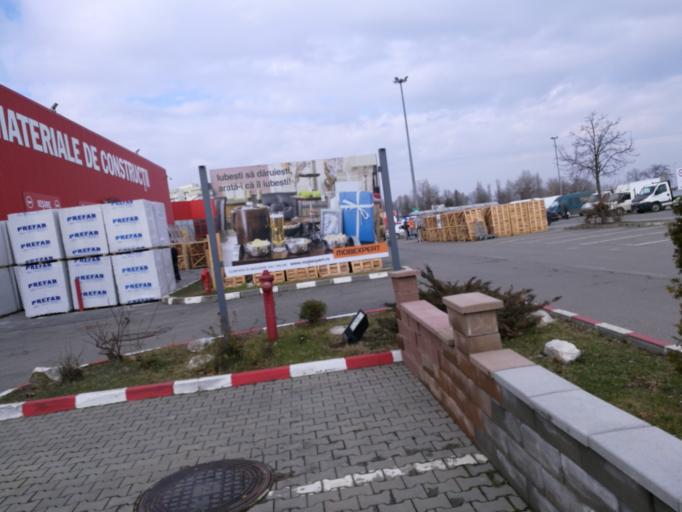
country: RO
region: Ilfov
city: Dobroesti
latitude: 44.4384
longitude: 26.1845
